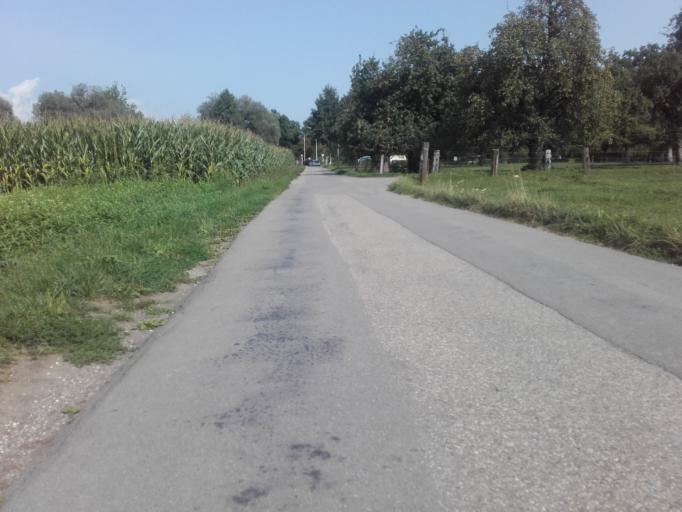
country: CH
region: Solothurn
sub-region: Bezirk Solothurn
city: Solothurn
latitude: 47.1991
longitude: 7.5219
